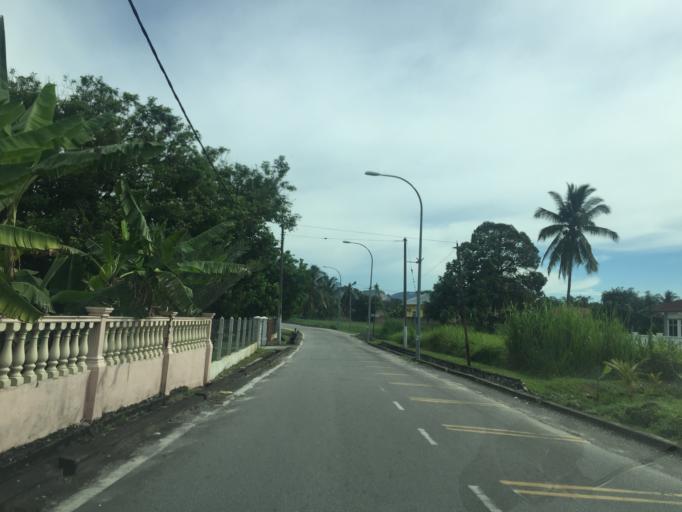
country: MY
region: Negeri Sembilan
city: Seremban
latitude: 2.7286
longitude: 101.9650
